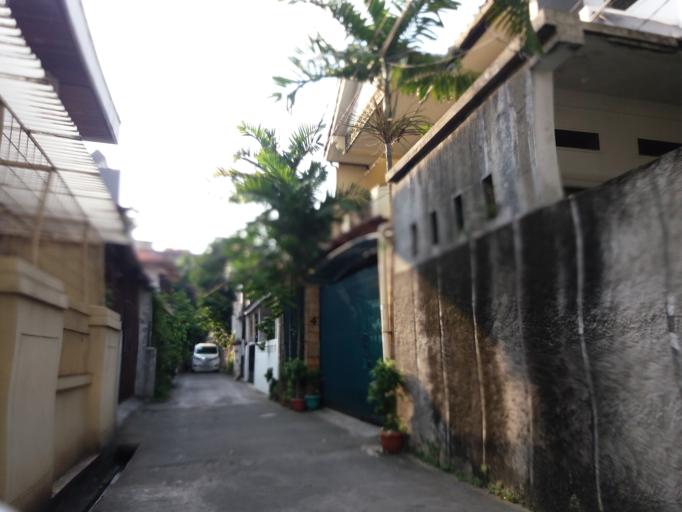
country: ID
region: Jakarta Raya
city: Jakarta
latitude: -6.2461
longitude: 106.8084
